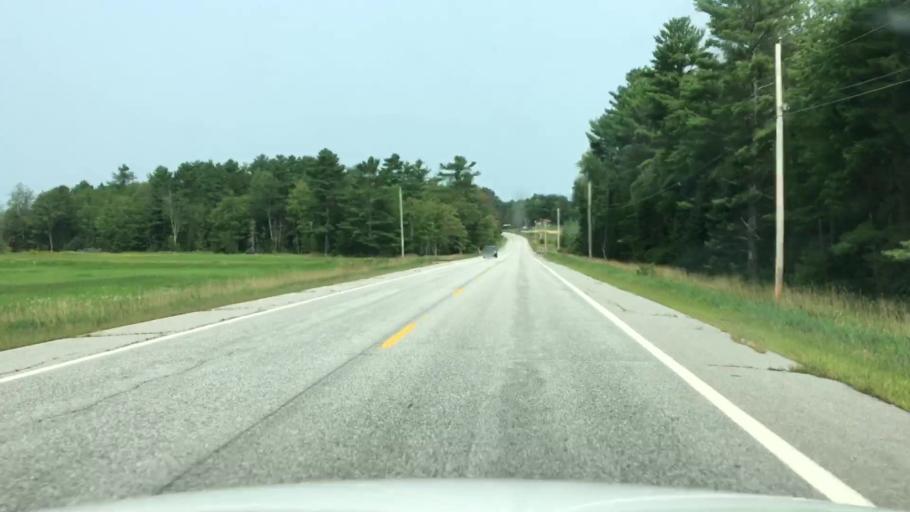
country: US
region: Maine
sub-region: Kennebec County
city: Wayne
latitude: 44.3917
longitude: -70.1139
